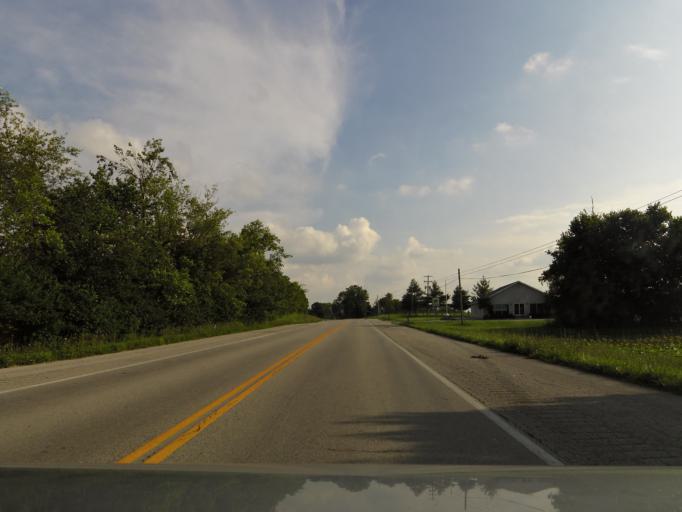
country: US
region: Kentucky
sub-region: Harrison County
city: Cynthiana
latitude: 38.2943
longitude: -84.3026
